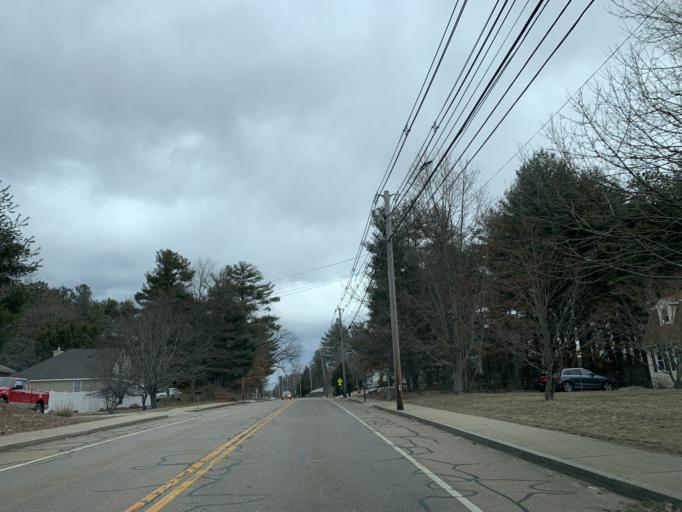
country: US
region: Massachusetts
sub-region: Norfolk County
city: Franklin
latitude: 42.0597
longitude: -71.4123
